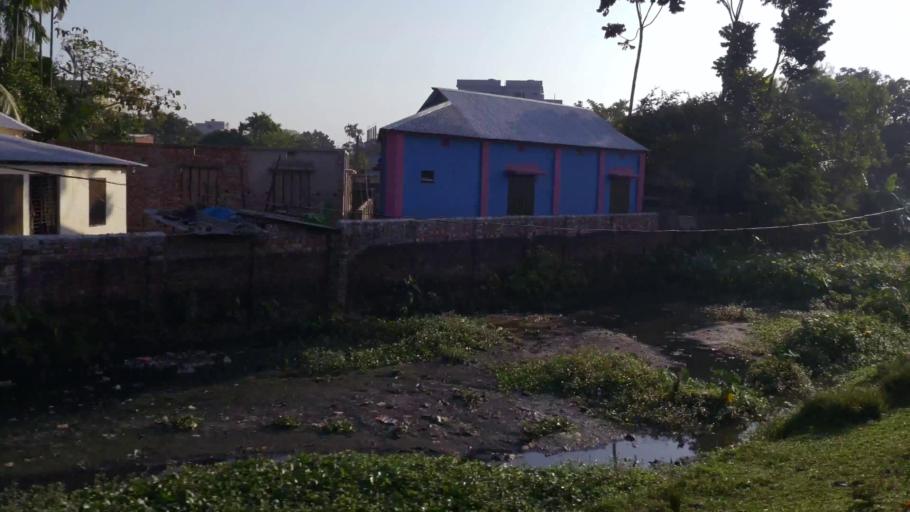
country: BD
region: Dhaka
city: Jamalpur
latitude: 24.8941
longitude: 89.9862
